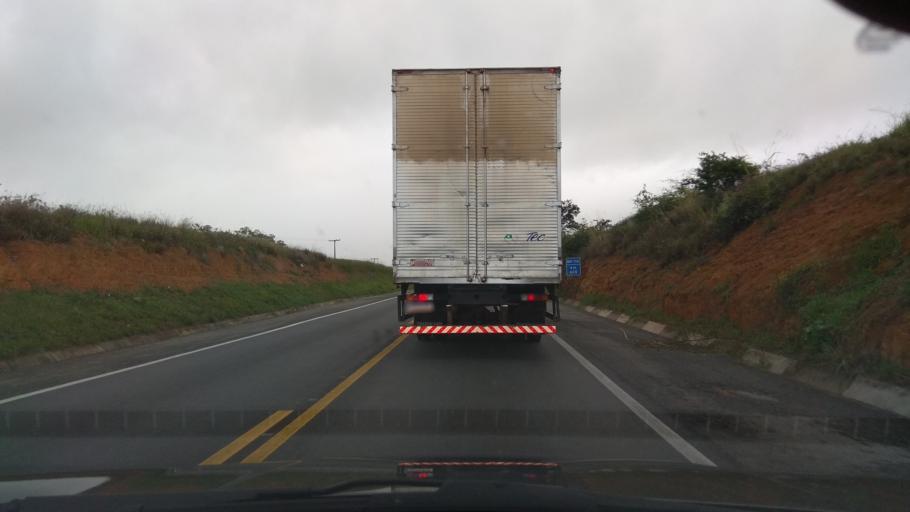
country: BR
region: Bahia
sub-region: Jaguaquara
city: Jaguaquara
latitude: -13.4780
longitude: -40.0410
